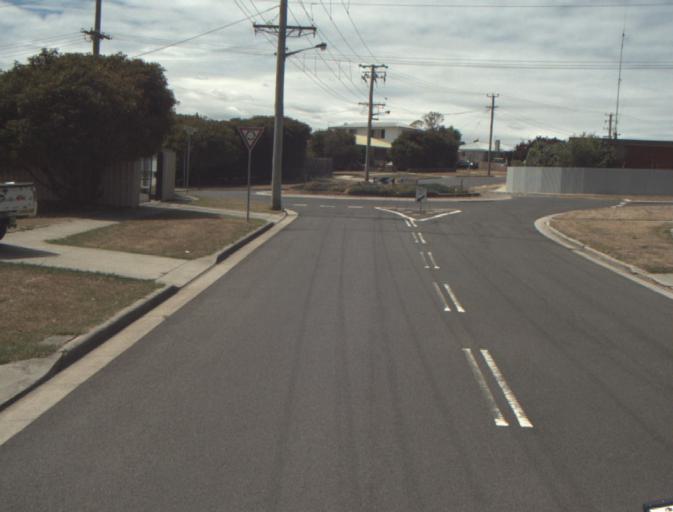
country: AU
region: Tasmania
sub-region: Launceston
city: Mayfield
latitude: -41.3829
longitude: 147.1180
